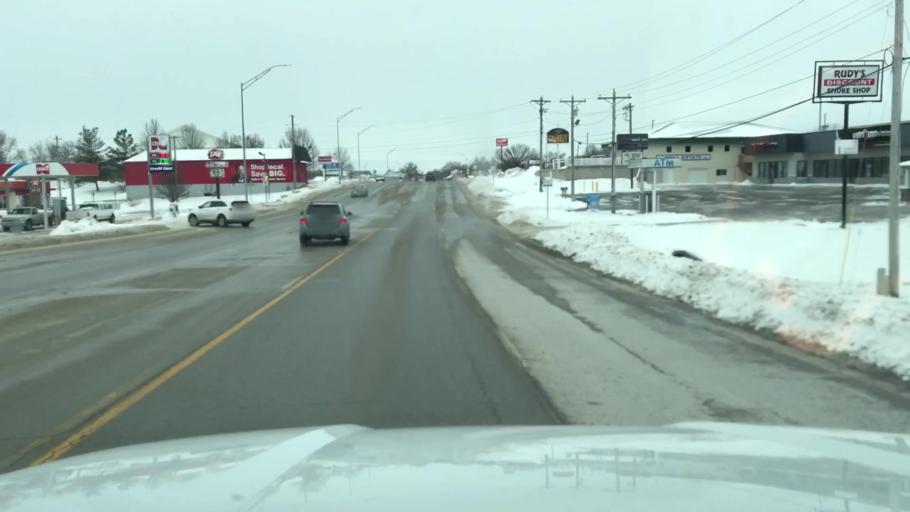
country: US
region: Missouri
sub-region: Clinton County
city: Cameron
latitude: 39.7516
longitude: -94.2345
